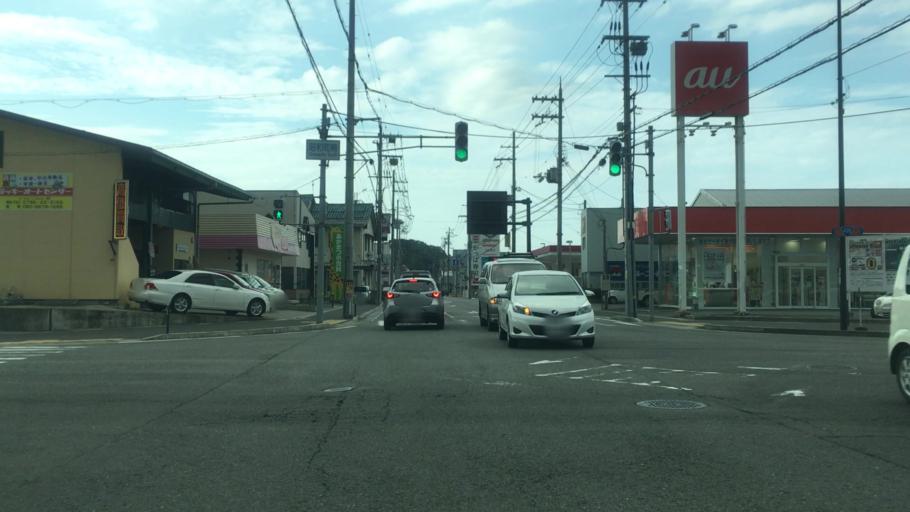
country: JP
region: Hyogo
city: Toyooka
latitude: 35.5280
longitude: 134.8205
